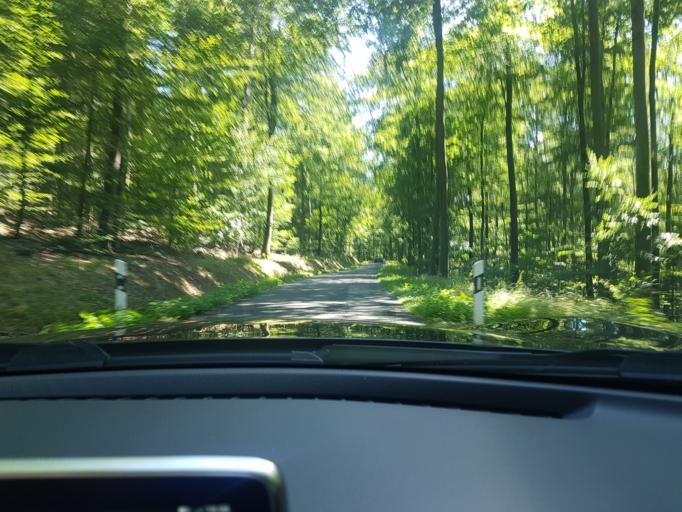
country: DE
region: Hesse
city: Hirschhorn
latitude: 49.3987
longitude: 8.8940
